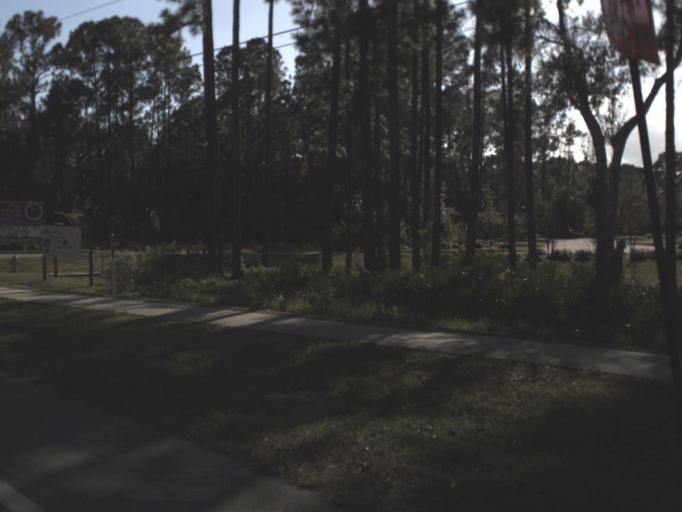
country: US
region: Florida
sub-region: Volusia County
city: Daytona Beach
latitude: 29.2007
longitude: -81.0870
